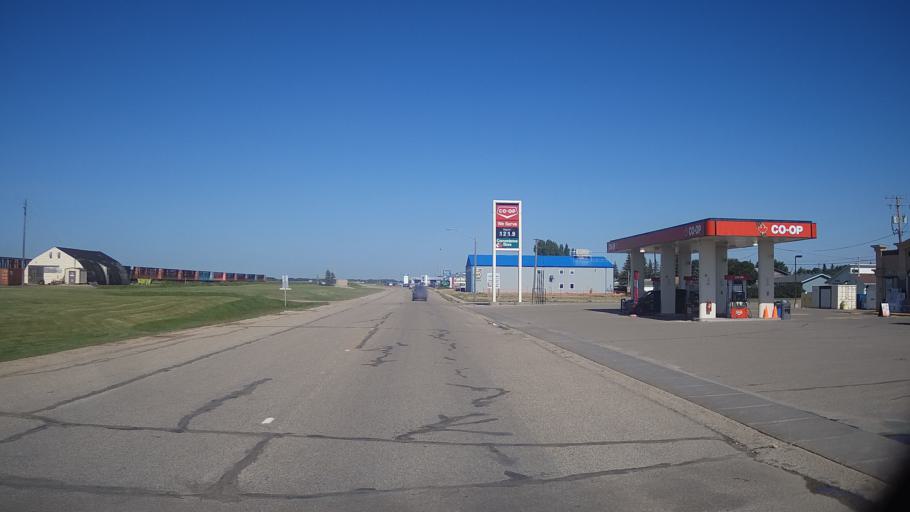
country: CA
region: Saskatchewan
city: Watrous
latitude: 51.6724
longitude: -105.4699
